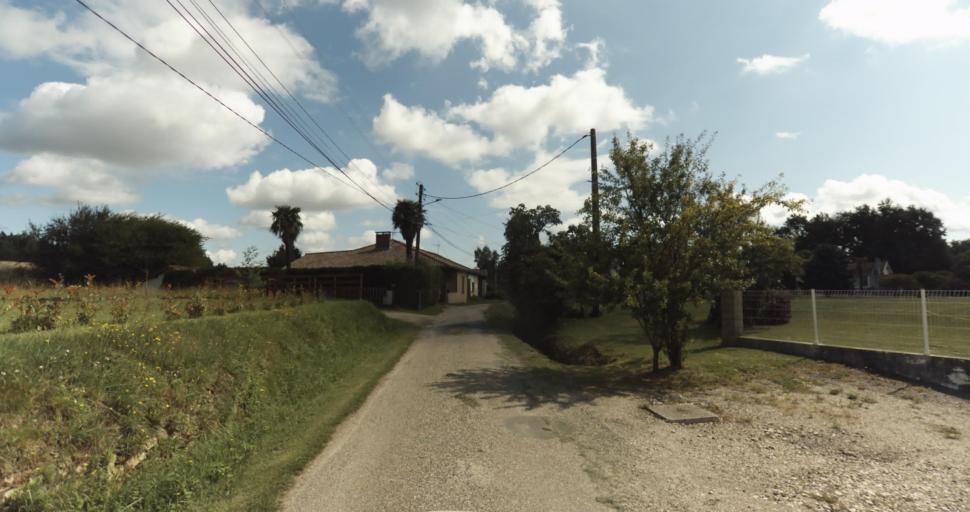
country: FR
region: Aquitaine
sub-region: Departement de la Gironde
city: Bazas
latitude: 44.4428
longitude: -0.1928
